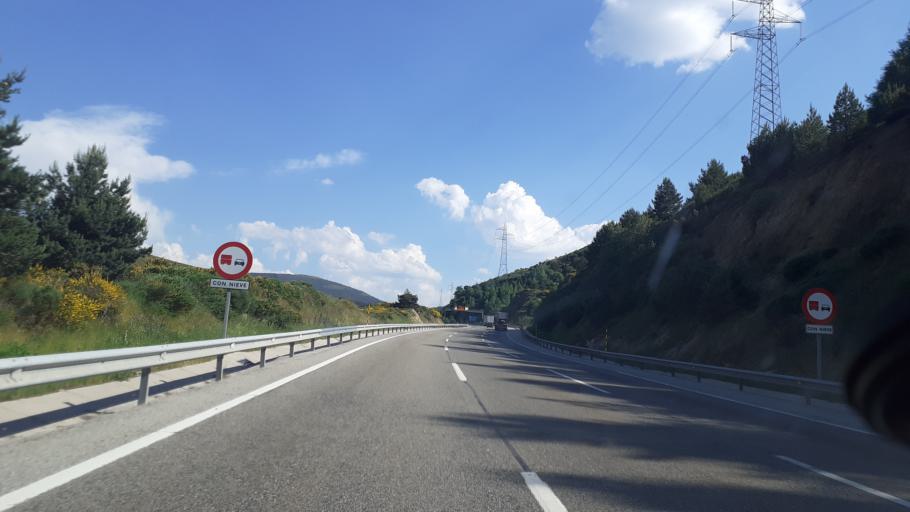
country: ES
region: Madrid
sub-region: Provincia de Madrid
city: Somosierra
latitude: 41.1550
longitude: -3.5854
